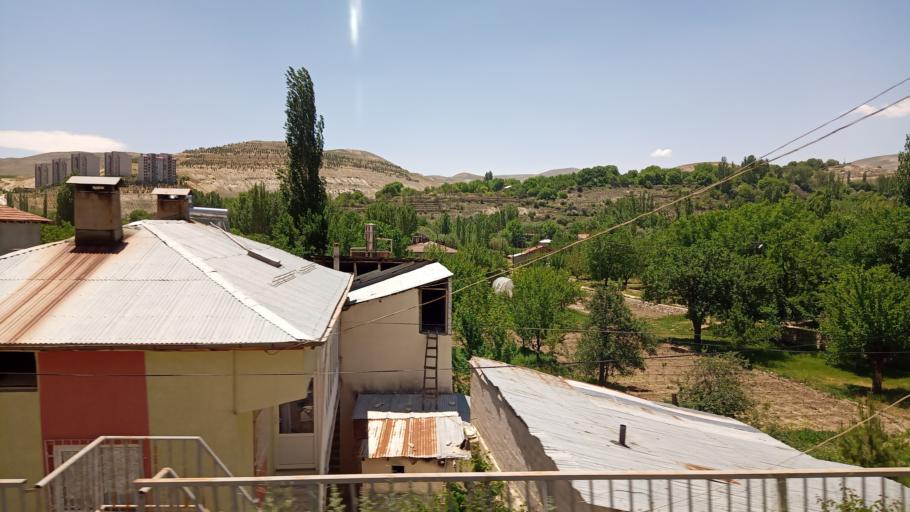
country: TR
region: Sivas
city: Gurun
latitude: 38.7235
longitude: 37.2852
